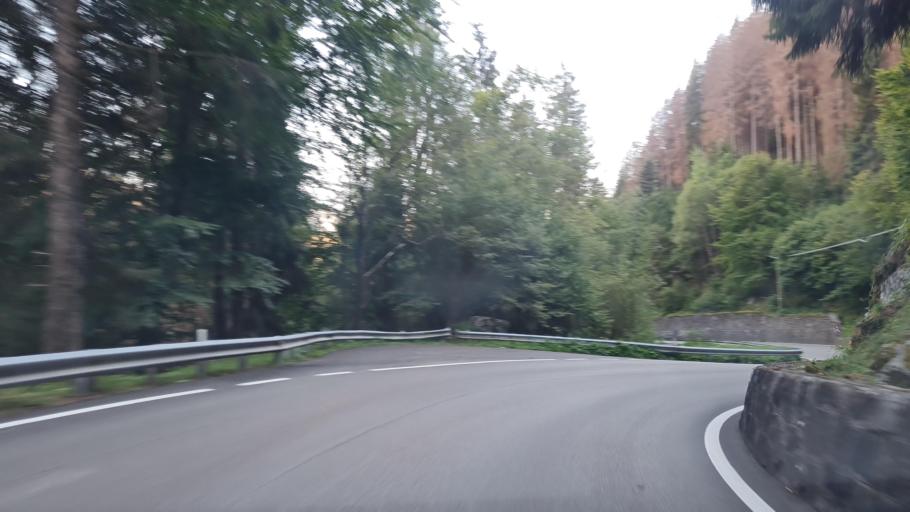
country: IT
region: Trentino-Alto Adige
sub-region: Provincia di Trento
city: Siror
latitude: 46.2197
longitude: 11.8121
